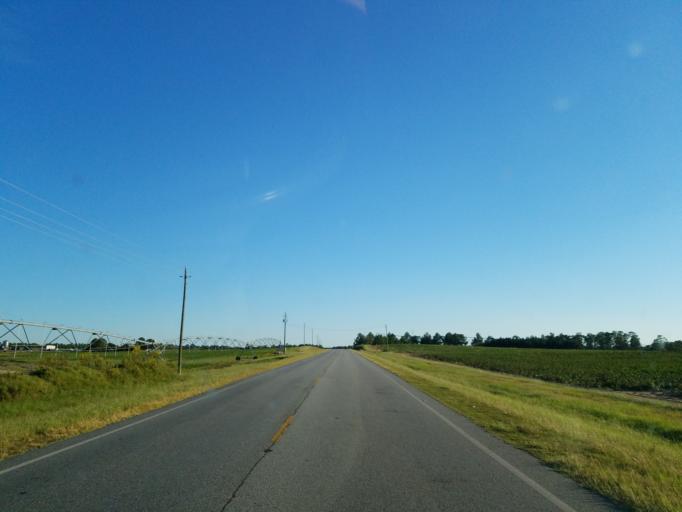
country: US
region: Georgia
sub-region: Worth County
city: Sylvester
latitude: 31.6159
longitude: -83.8647
